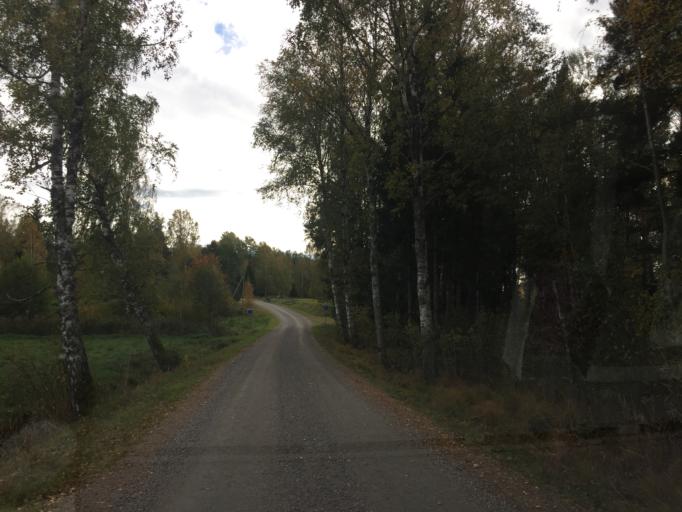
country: SE
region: Soedermanland
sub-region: Vingakers Kommun
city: Vingaker
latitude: 58.9980
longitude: 15.7391
